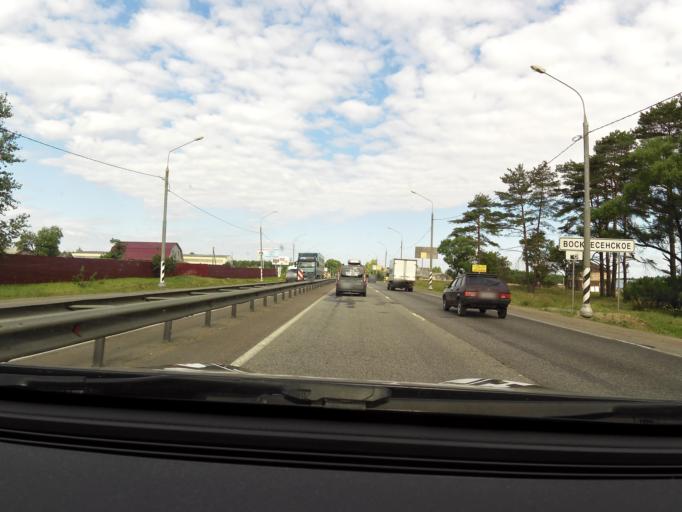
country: RU
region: Tverskaya
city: Gorodnya
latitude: 56.7376
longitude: 36.2520
